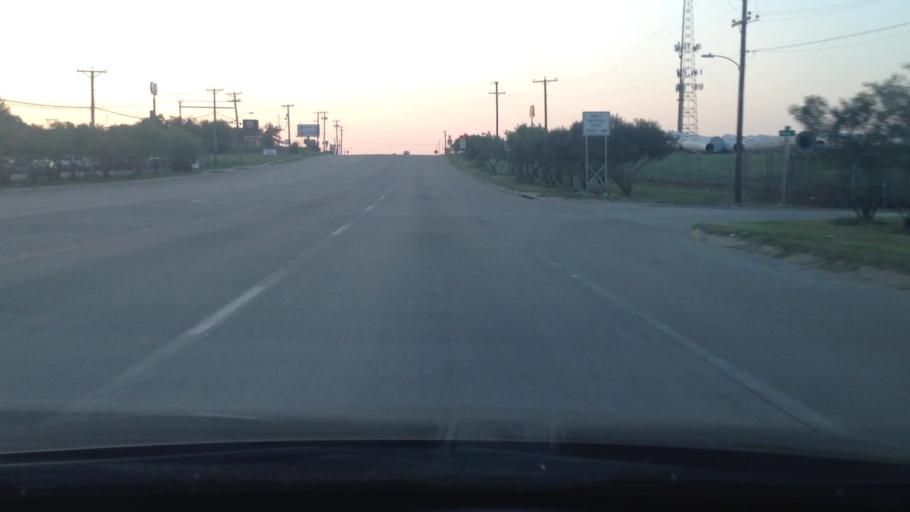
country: US
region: Texas
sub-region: Tarrant County
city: Kennedale
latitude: 32.6621
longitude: -97.2376
